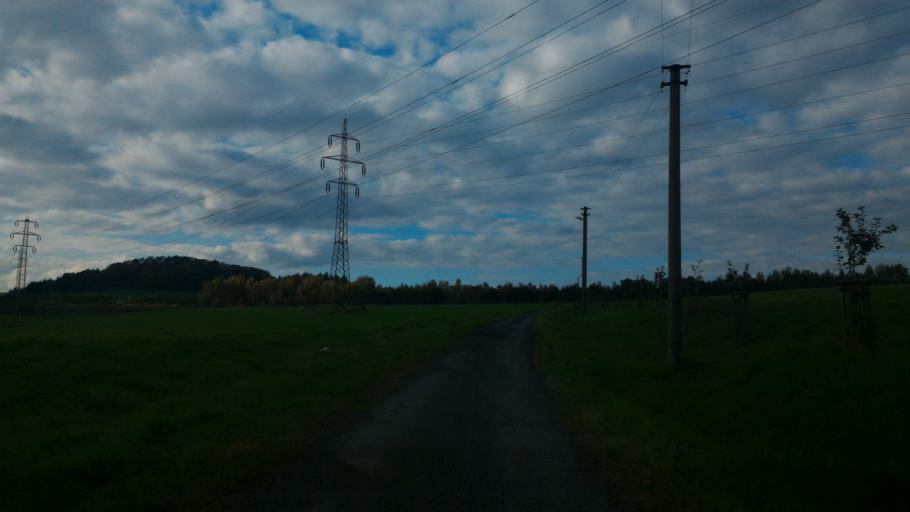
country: CZ
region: Ustecky
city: Ceska Kamenice
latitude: 50.7913
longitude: 14.3669
